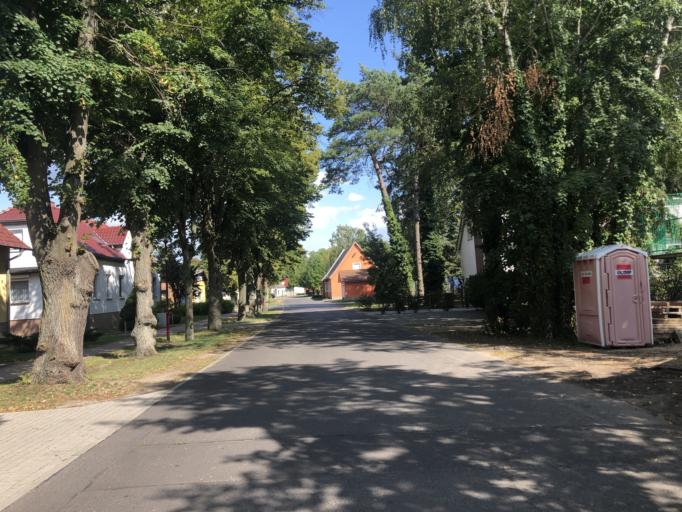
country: DE
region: Brandenburg
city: Mullrose
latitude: 52.2423
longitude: 14.4105
